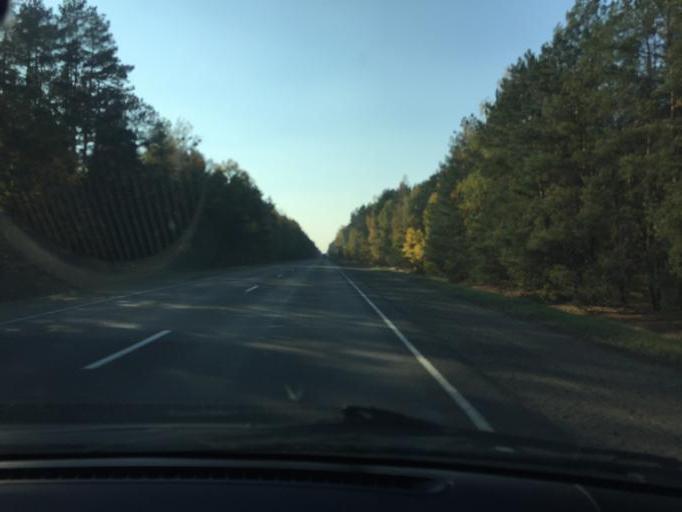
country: BY
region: Brest
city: Mikashevichy
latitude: 52.2408
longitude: 27.3101
